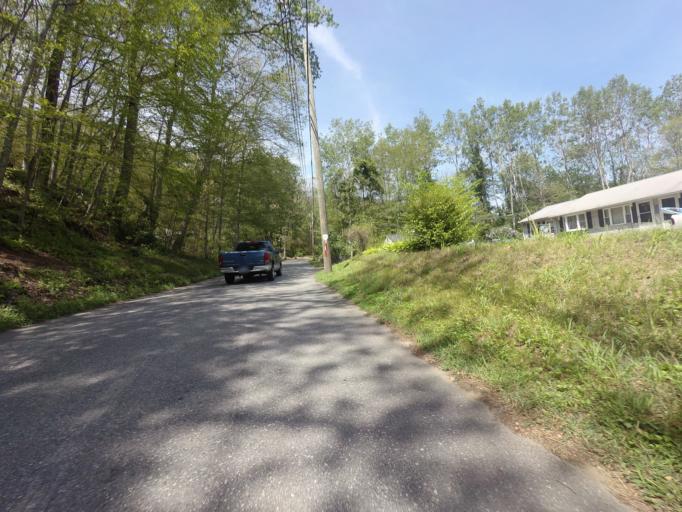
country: US
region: Connecticut
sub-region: Windham County
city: East Brooklyn
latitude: 41.8364
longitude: -71.9357
